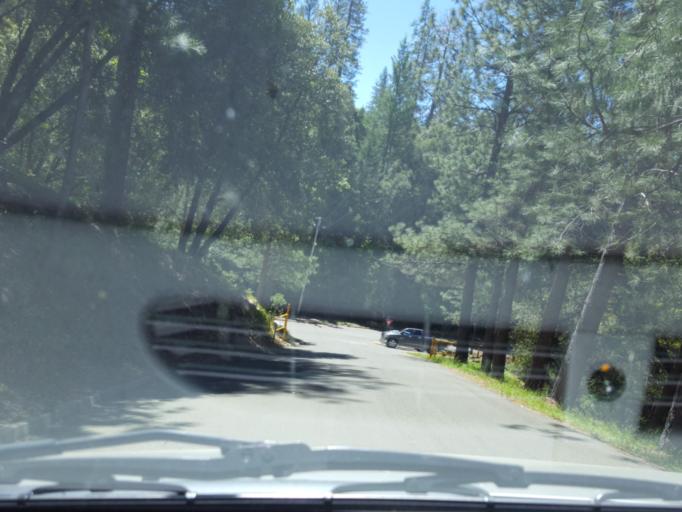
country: US
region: California
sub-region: El Dorado County
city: Placerville
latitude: 38.7436
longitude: -120.8002
